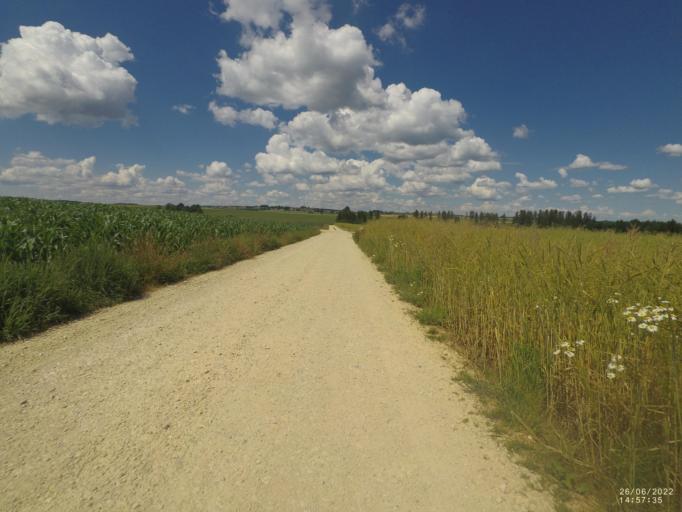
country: DE
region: Baden-Wuerttemberg
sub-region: Regierungsbezirk Stuttgart
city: Bohmenkirch
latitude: 48.6637
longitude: 9.9333
